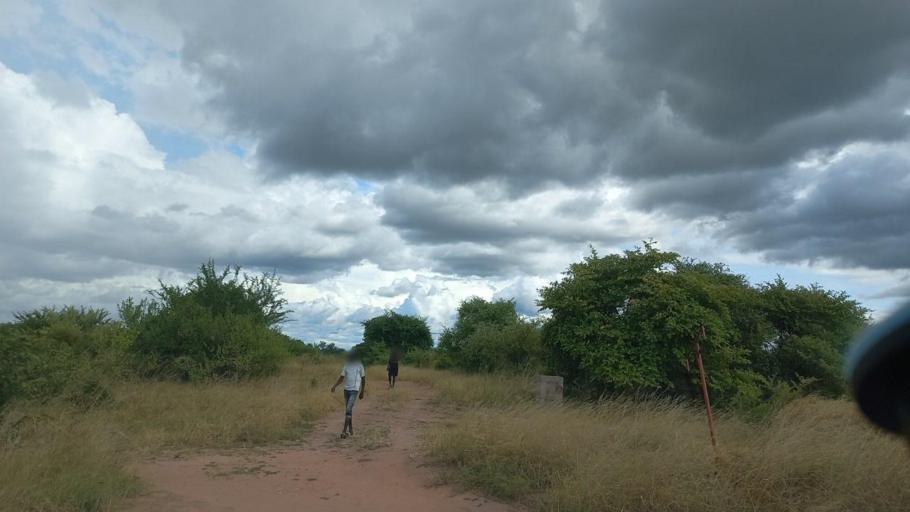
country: ZM
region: Lusaka
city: Luangwa
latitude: -15.6408
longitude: 30.3847
